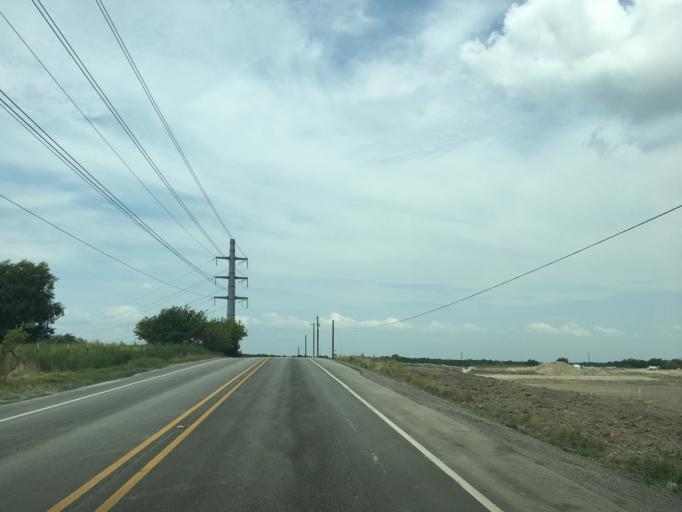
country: US
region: Texas
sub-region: Rockwall County
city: Rockwall
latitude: 32.9365
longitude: -96.4376
